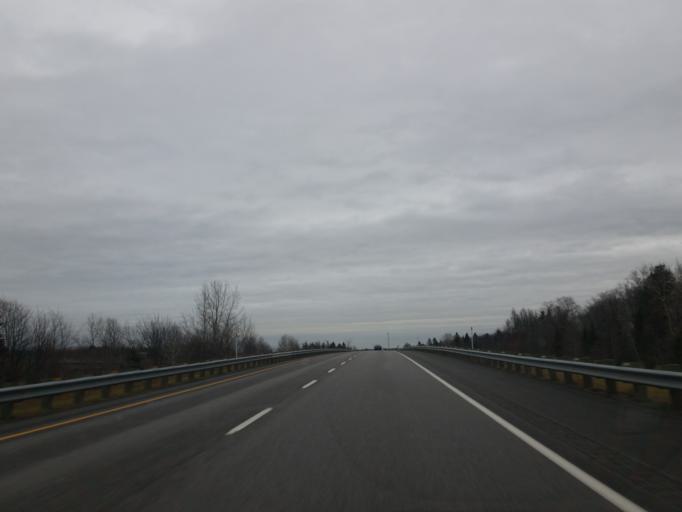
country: CA
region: Quebec
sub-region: Capitale-Nationale
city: Saint-Marc-des-Carrieres
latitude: 46.6465
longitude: -71.9875
